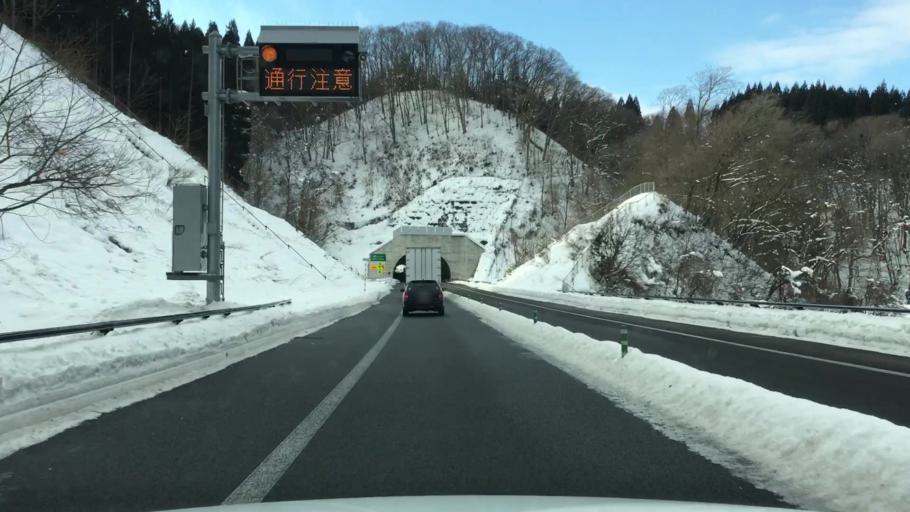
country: JP
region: Akita
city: Takanosu
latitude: 40.2236
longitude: 140.4325
